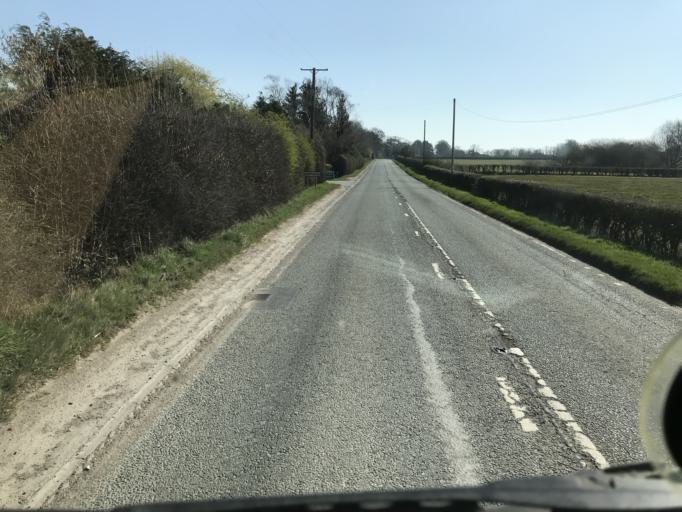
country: GB
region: England
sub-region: Cheshire East
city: Mobberley
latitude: 53.2807
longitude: -2.3094
